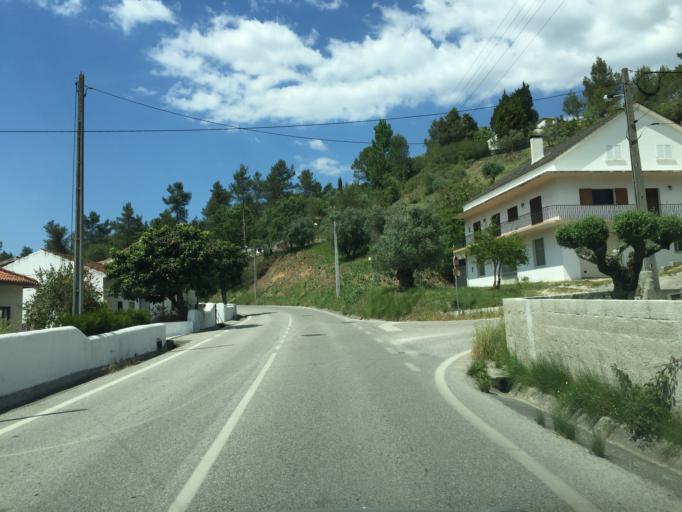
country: PT
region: Santarem
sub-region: Ourem
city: Ourem
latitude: 39.6649
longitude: -8.5716
